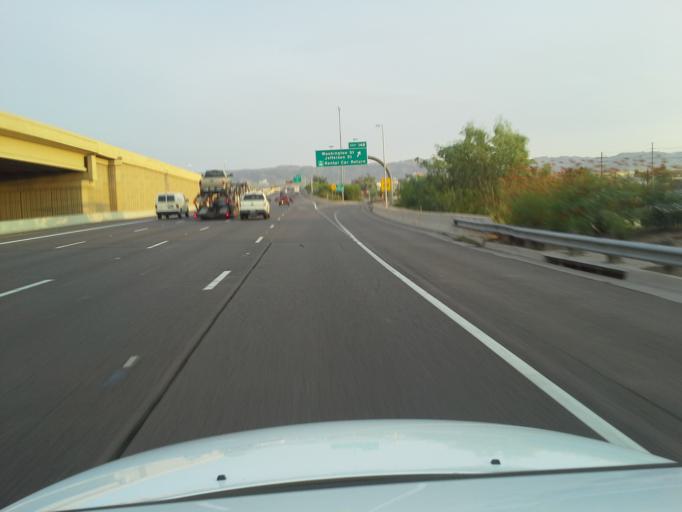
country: US
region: Arizona
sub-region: Maricopa County
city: Phoenix
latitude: 33.4520
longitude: -112.0376
